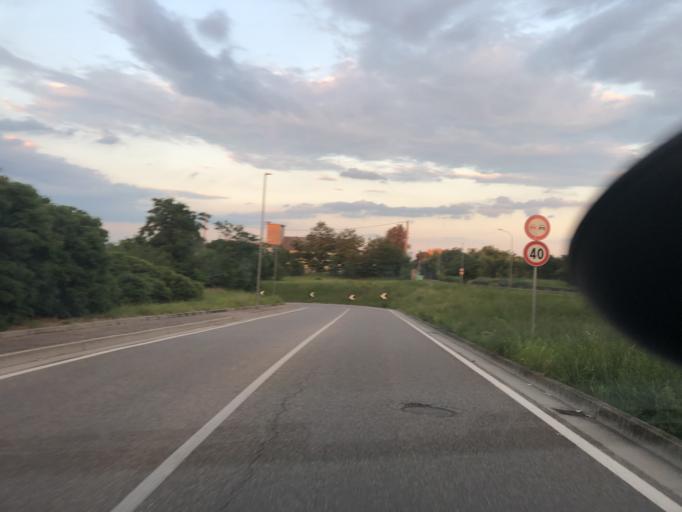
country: IT
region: Veneto
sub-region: Provincia di Verona
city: Bussolengo
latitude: 45.4737
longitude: 10.8573
